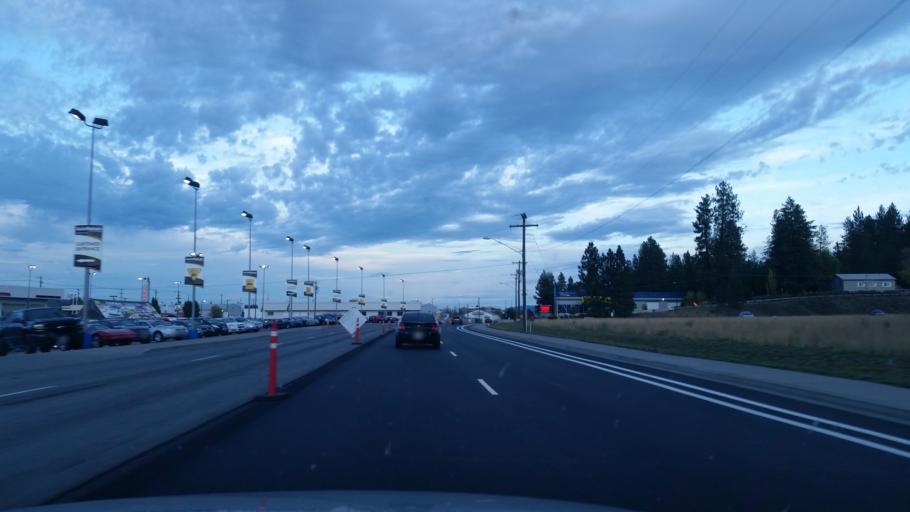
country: US
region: Washington
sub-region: Spokane County
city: Dishman
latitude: 47.6551
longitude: -117.2915
